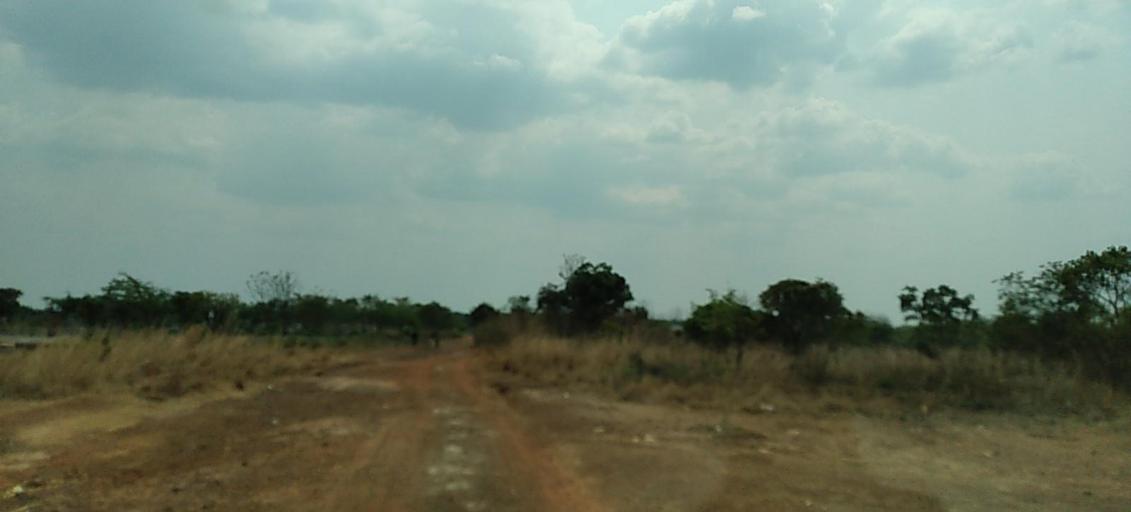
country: ZM
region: Copperbelt
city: Kalulushi
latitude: -12.8739
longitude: 28.0771
